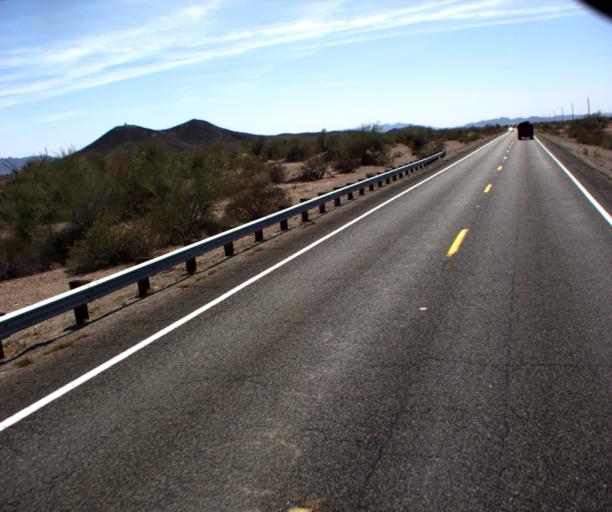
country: US
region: Arizona
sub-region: Yuma County
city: Fortuna Foothills
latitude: 32.9393
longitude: -114.3073
